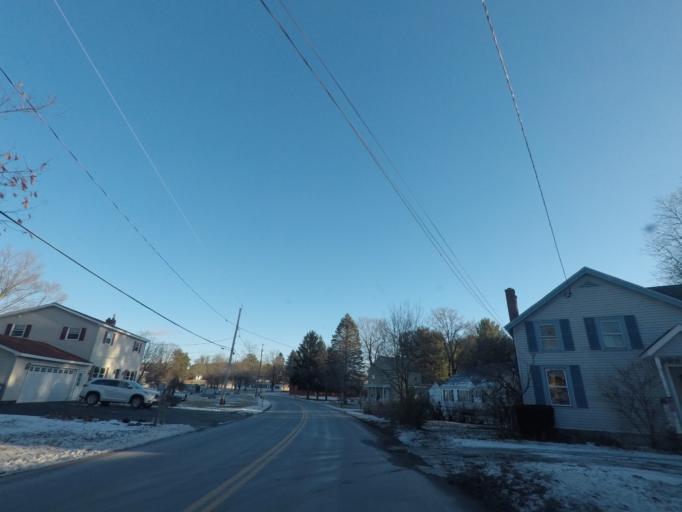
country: US
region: New York
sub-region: Rensselaer County
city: Poestenkill
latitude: 42.7286
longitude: -73.5998
